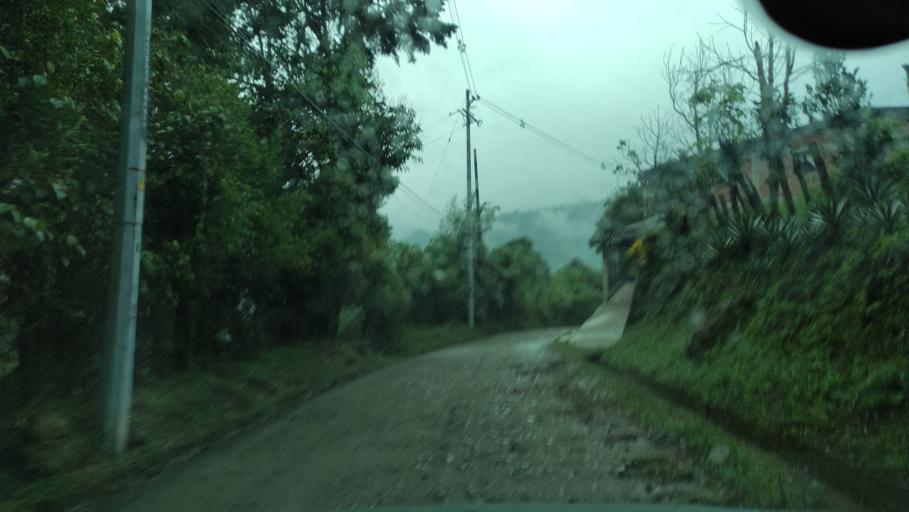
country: CO
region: Valle del Cauca
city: Jamundi
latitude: 3.3271
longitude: -76.6316
